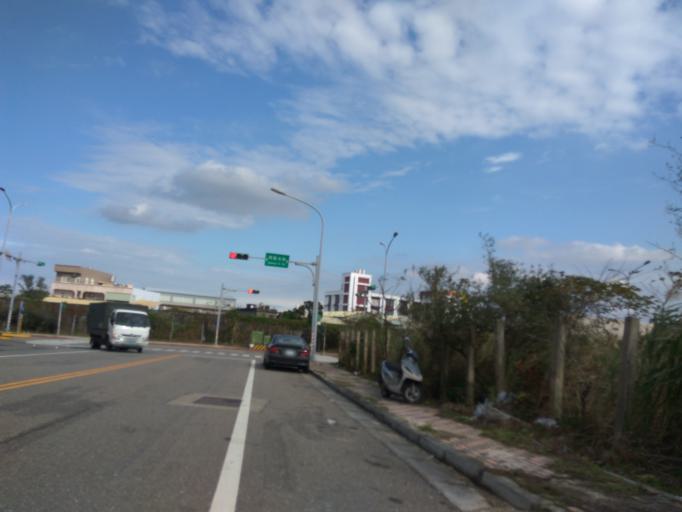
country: TW
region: Taiwan
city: Taoyuan City
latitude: 25.0593
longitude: 121.1788
